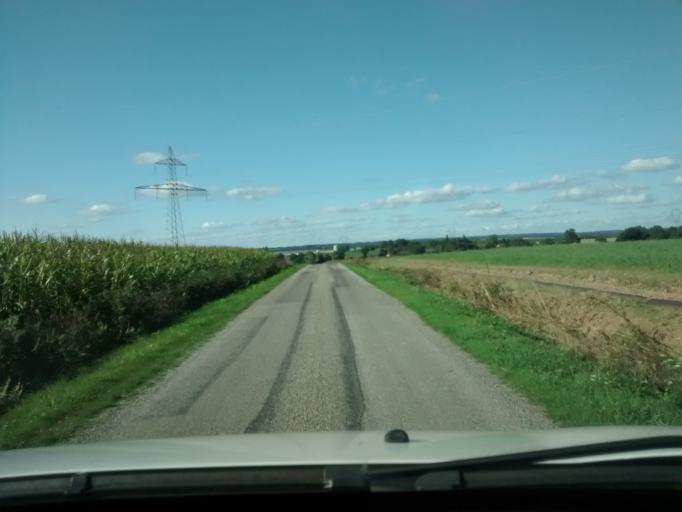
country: FR
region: Brittany
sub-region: Departement d'Ille-et-Vilaine
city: Noyal-sur-Vilaine
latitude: 48.1019
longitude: -1.5607
